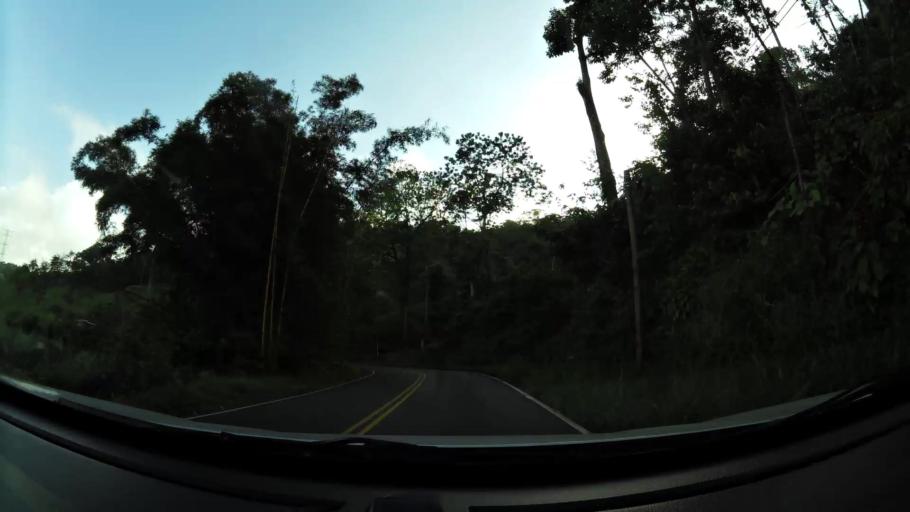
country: CR
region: Limon
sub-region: Canton de Siquirres
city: Siquirres
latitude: 10.0529
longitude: -83.5517
